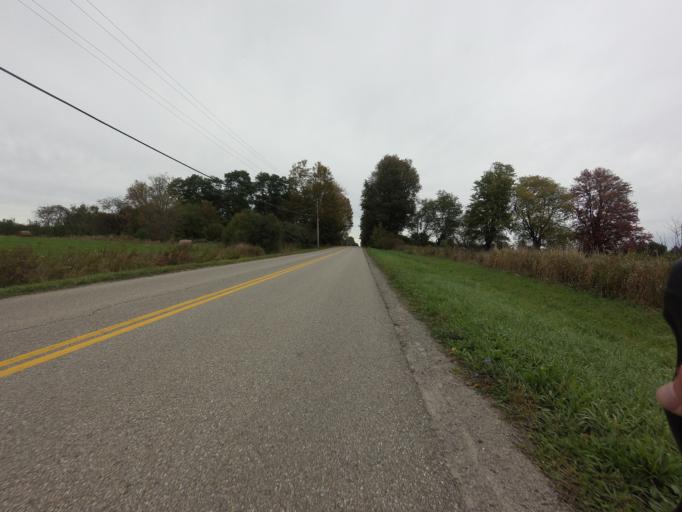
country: CA
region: Ontario
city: Brockville
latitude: 44.6642
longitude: -75.8790
